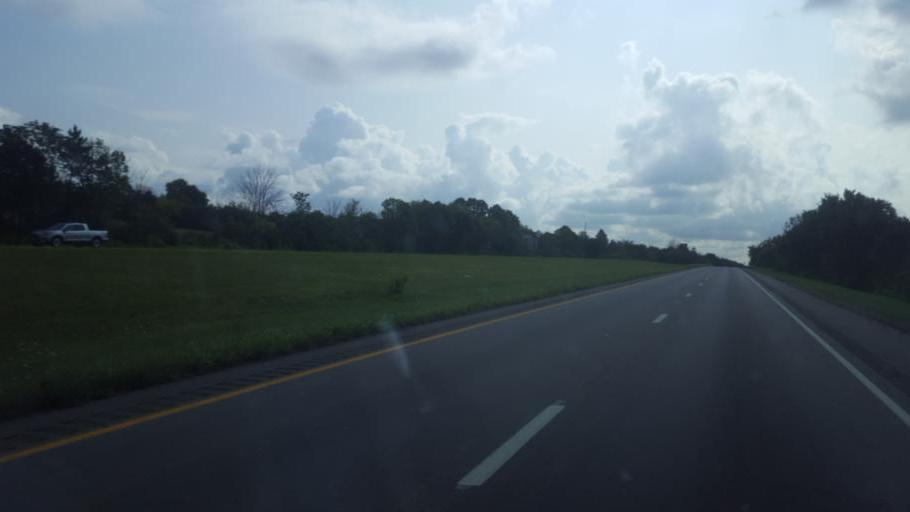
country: US
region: Ohio
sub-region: Stark County
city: Massillon
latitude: 40.7617
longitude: -81.5620
